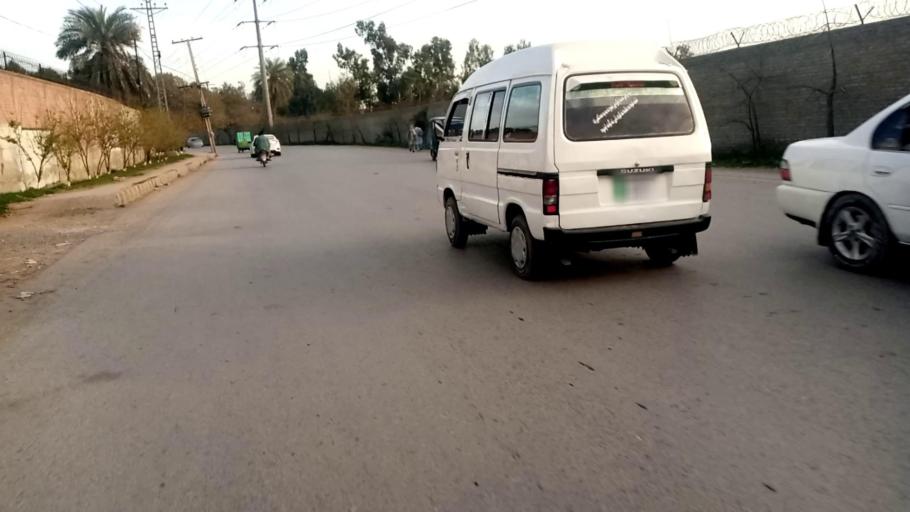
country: PK
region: Khyber Pakhtunkhwa
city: Peshawar
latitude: 34.0214
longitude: 71.5643
